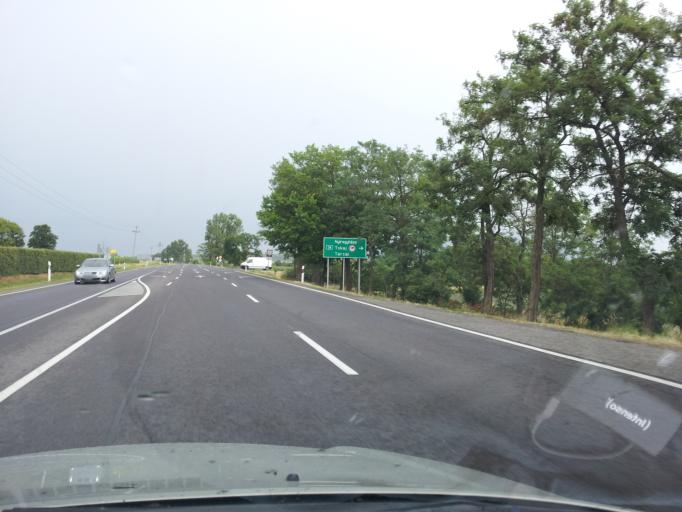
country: HU
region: Borsod-Abauj-Zemplen
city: Mad
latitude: 48.1650
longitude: 21.3034
